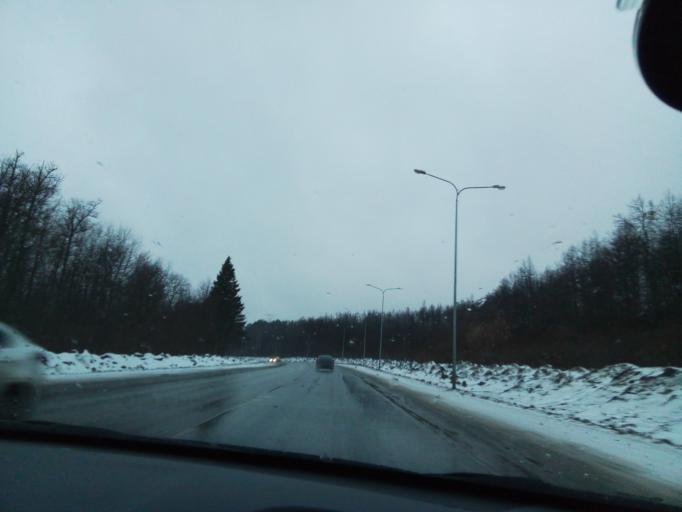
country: RU
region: Chuvashia
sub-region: Cheboksarskiy Rayon
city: Cheboksary
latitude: 56.1353
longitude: 47.1753
